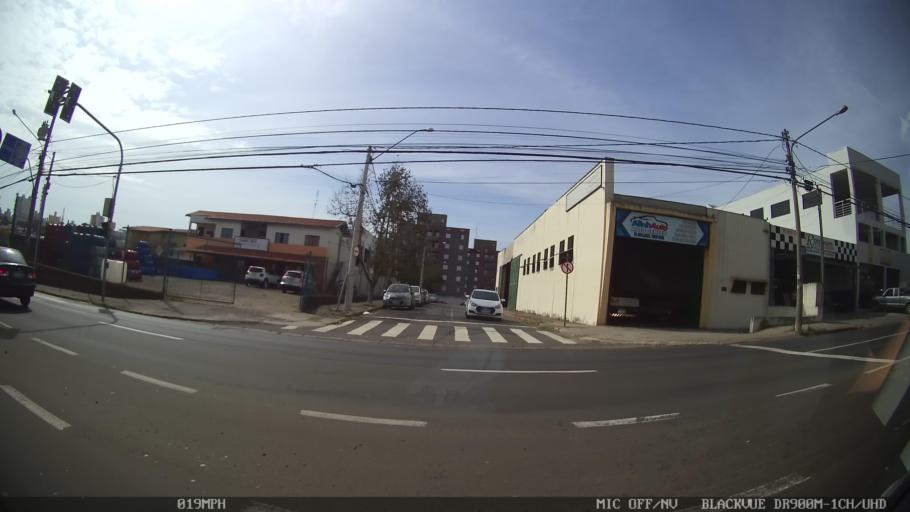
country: BR
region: Sao Paulo
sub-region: Piracicaba
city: Piracicaba
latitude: -22.7472
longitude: -47.6383
